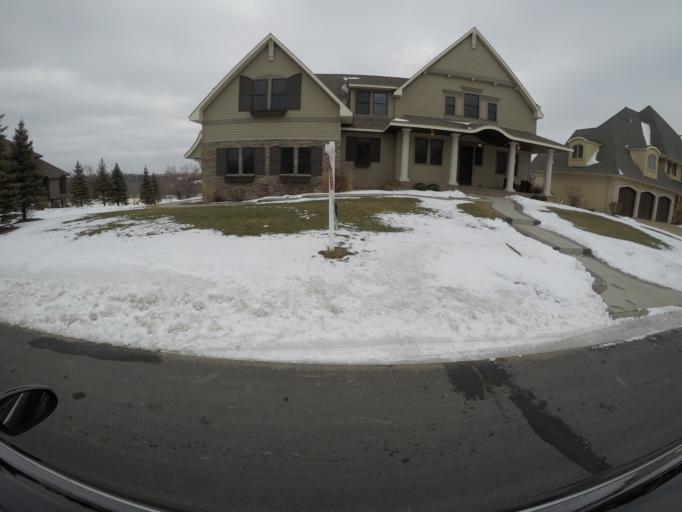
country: US
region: Minnesota
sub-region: Hennepin County
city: Eden Prairie
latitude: 44.8273
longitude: -93.4914
